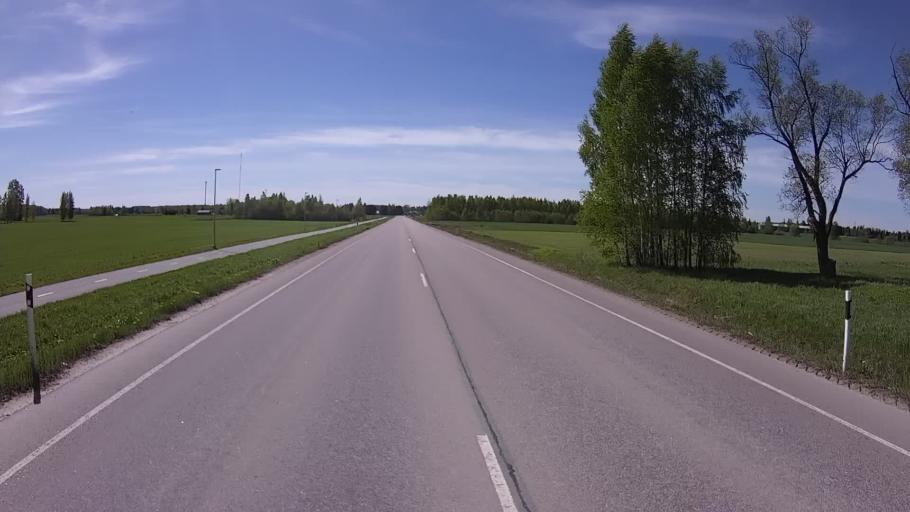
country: EE
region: Polvamaa
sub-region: Polva linn
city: Polva
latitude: 58.0796
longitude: 27.0895
